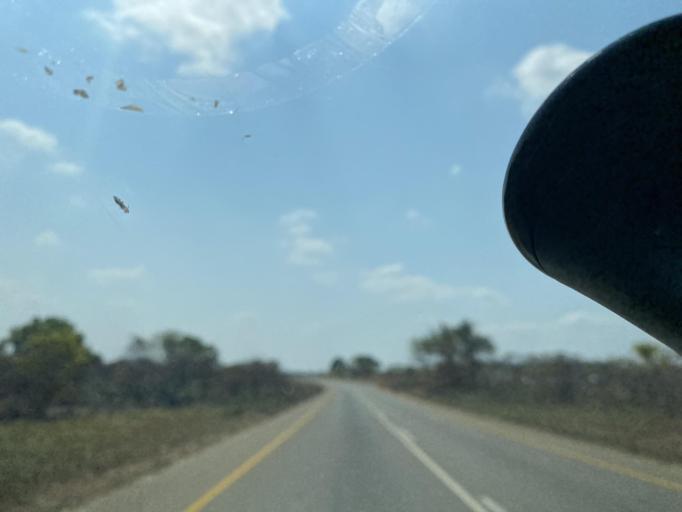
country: ZM
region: Lusaka
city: Chongwe
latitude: -15.5443
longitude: 28.6653
